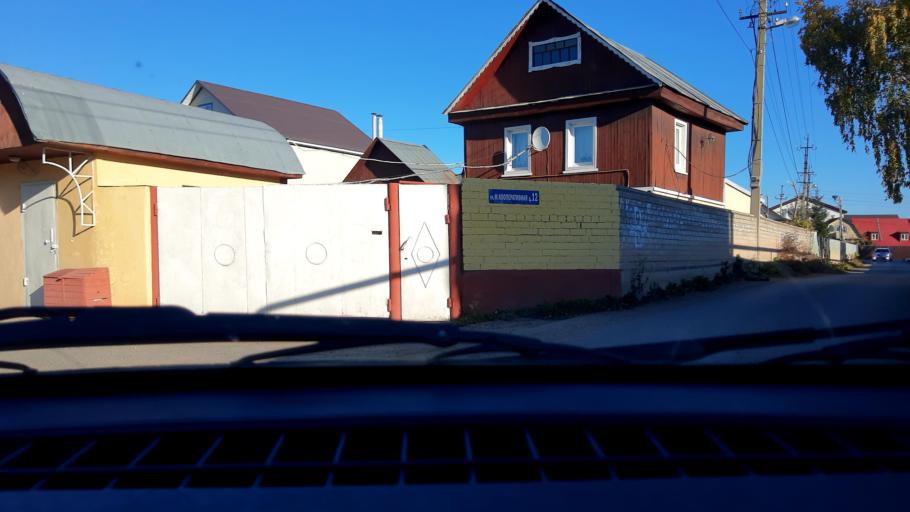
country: RU
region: Bashkortostan
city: Ufa
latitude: 54.6931
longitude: 55.9476
